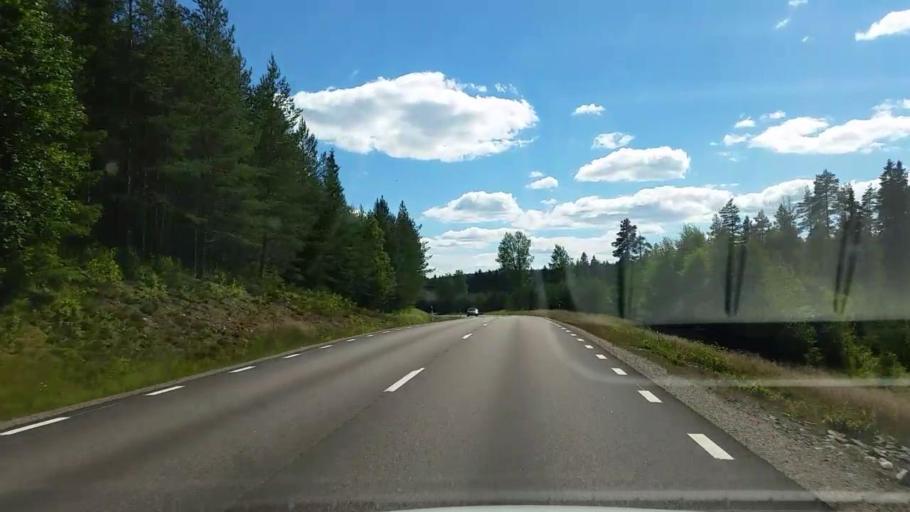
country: SE
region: Dalarna
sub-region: Faluns Kommun
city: Svardsjo
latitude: 60.7636
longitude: 15.7543
